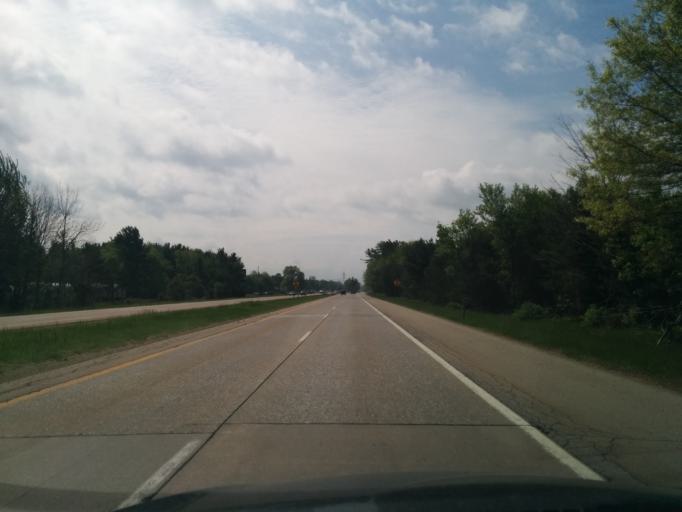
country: US
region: Michigan
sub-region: Ottawa County
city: Grand Haven
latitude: 43.0126
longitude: -86.2079
